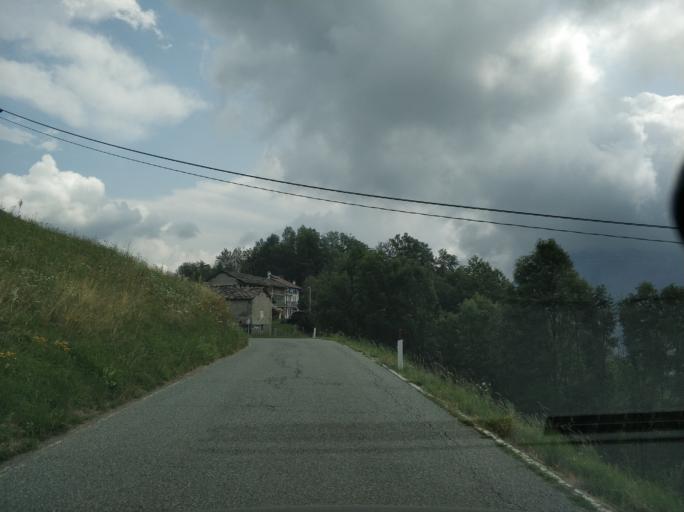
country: IT
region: Piedmont
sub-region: Provincia di Torino
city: Viu
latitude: 45.1970
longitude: 7.3707
